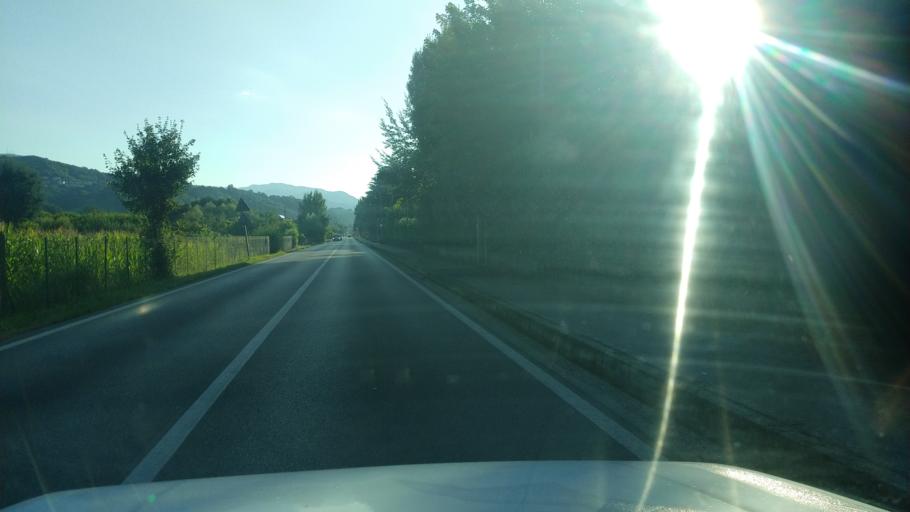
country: IT
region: Veneto
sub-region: Provincia di Vicenza
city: Pianezze
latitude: 45.7313
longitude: 11.6304
